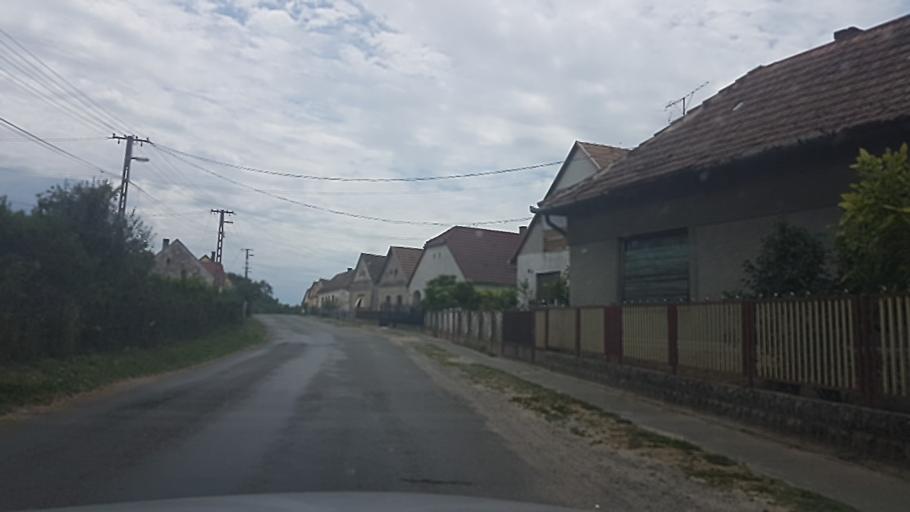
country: HU
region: Somogy
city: Barcs
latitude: 45.9734
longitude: 17.5894
